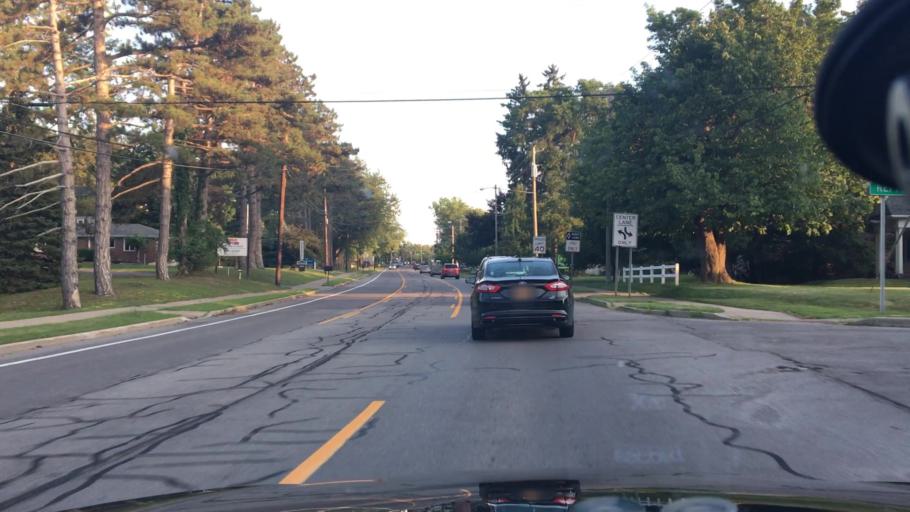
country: US
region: New York
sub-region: Erie County
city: Orchard Park
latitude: 42.7923
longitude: -78.7517
